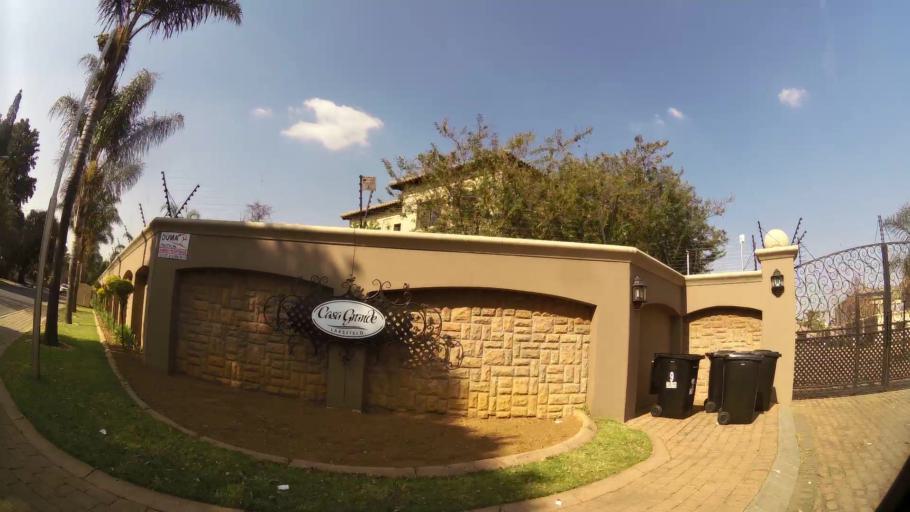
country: ZA
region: Gauteng
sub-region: Ekurhuleni Metropolitan Municipality
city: Boksburg
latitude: -26.1854
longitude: 28.2829
